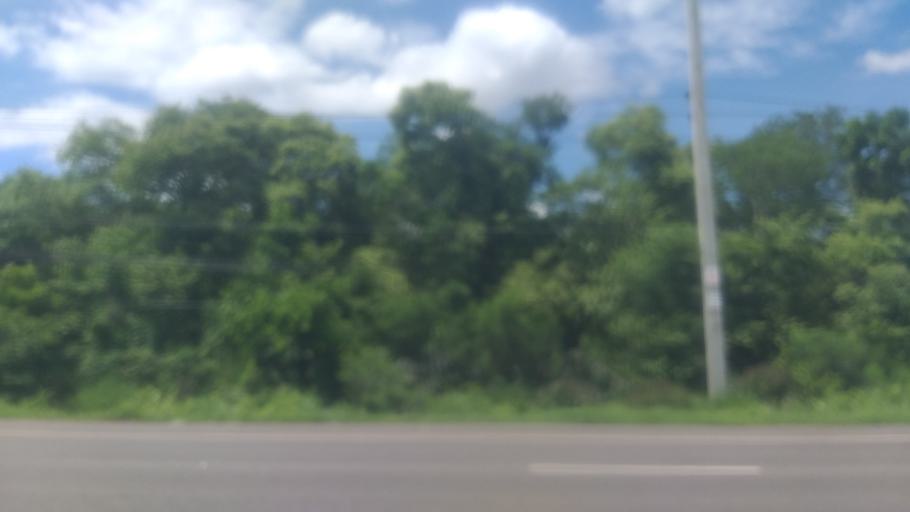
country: TH
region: Nakhon Ratchasima
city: Phra Thong Kham
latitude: 15.3021
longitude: 101.9776
